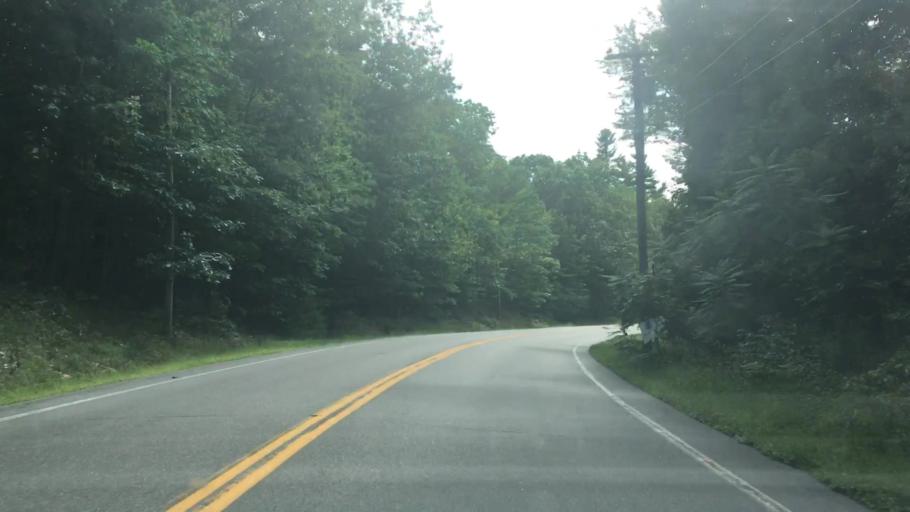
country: US
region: Maine
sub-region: Androscoggin County
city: Poland
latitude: 43.9981
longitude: -70.4644
